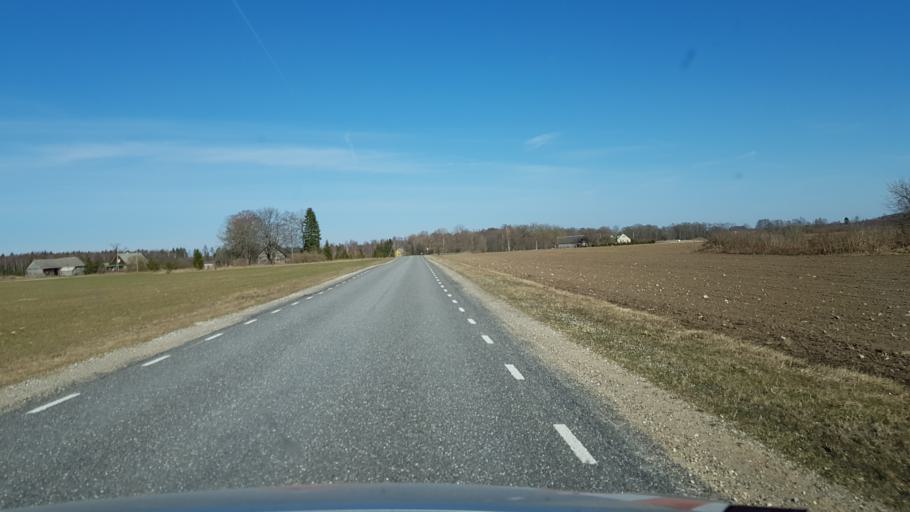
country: EE
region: Jaervamaa
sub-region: Koeru vald
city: Koeru
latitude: 59.0067
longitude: 26.0972
